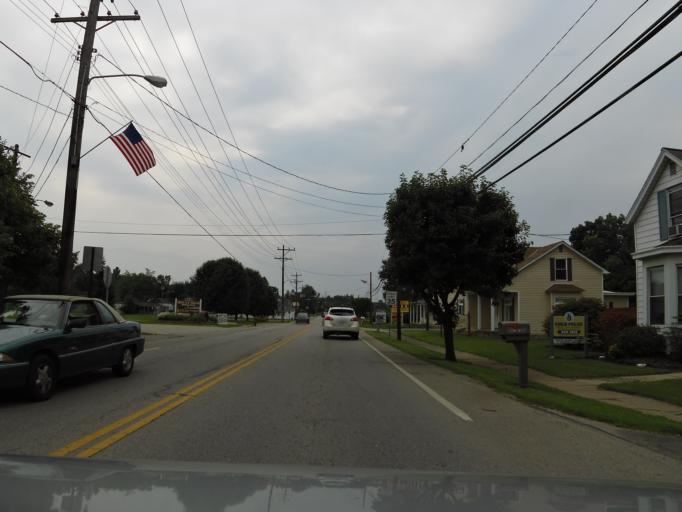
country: US
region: Ohio
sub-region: Brown County
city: Mount Orab
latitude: 39.0259
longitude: -83.9202
